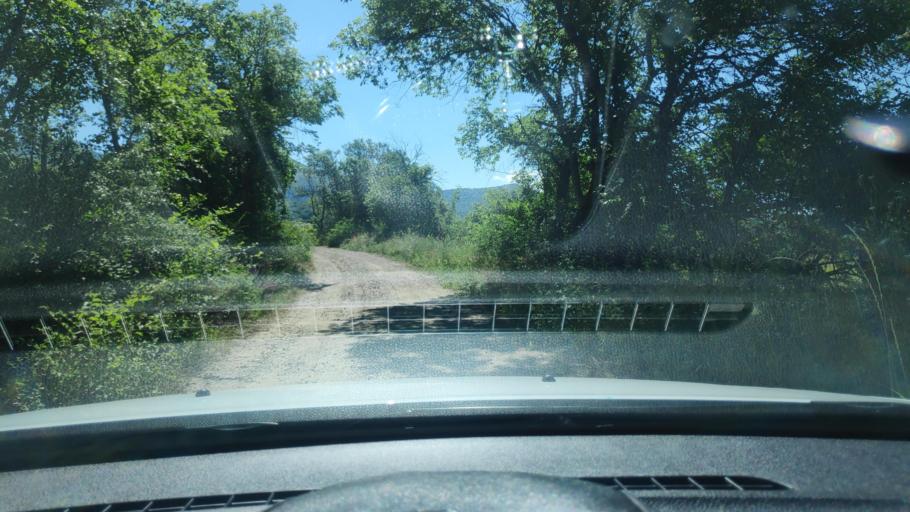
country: MK
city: Klechovce
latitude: 42.0708
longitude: 21.8841
